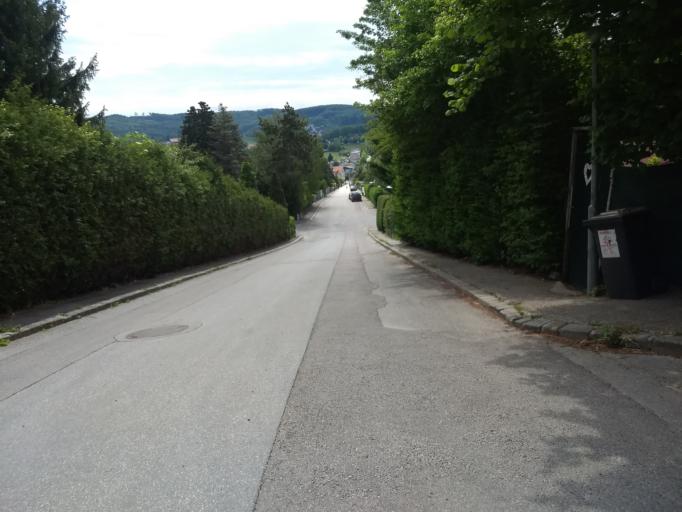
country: AT
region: Lower Austria
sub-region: Politischer Bezirk Wien-Umgebung
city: Gablitz
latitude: 48.2338
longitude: 16.1507
